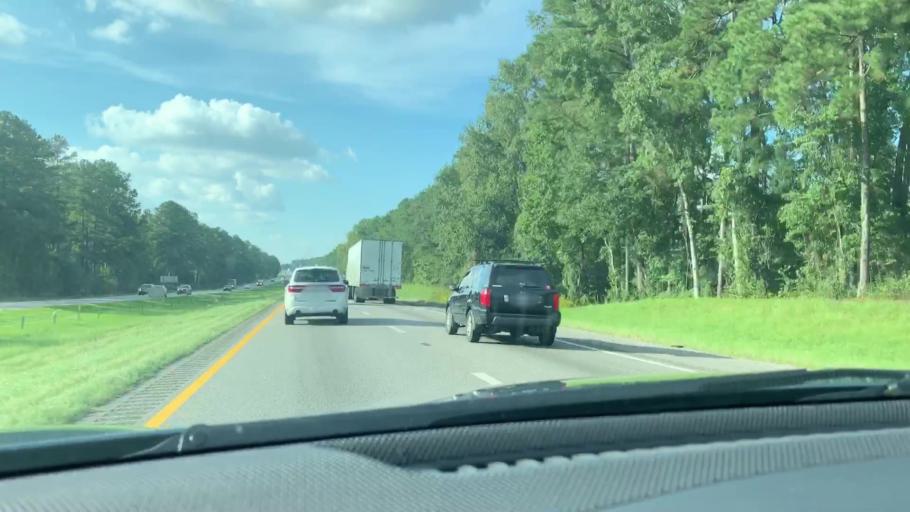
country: US
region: South Carolina
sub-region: Orangeburg County
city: Brookdale
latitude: 33.5457
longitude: -80.8129
